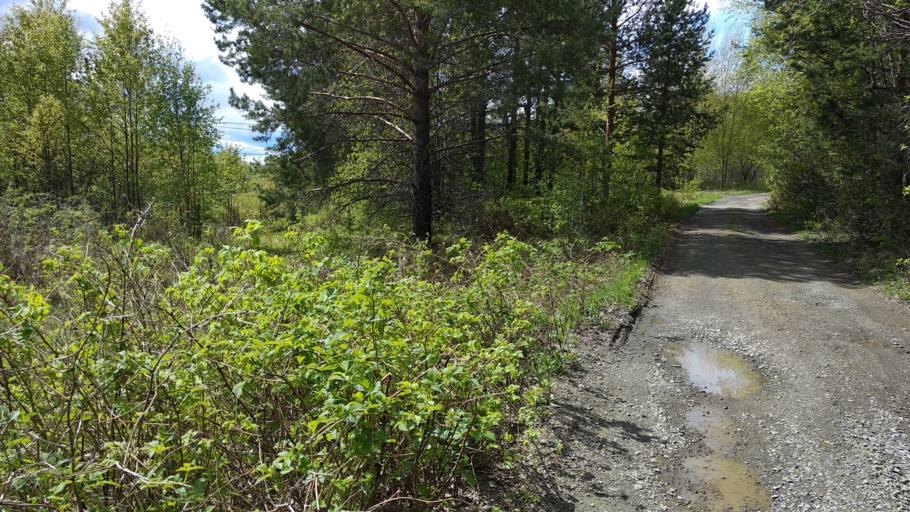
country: RU
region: Sverdlovsk
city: Krasnotur'insk
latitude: 59.7885
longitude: 60.1500
